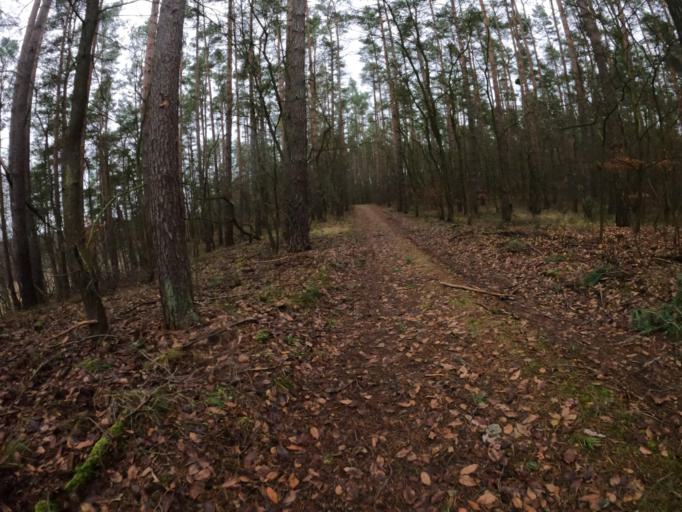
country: PL
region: West Pomeranian Voivodeship
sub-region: Powiat mysliborski
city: Debno
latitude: 52.7296
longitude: 14.7543
